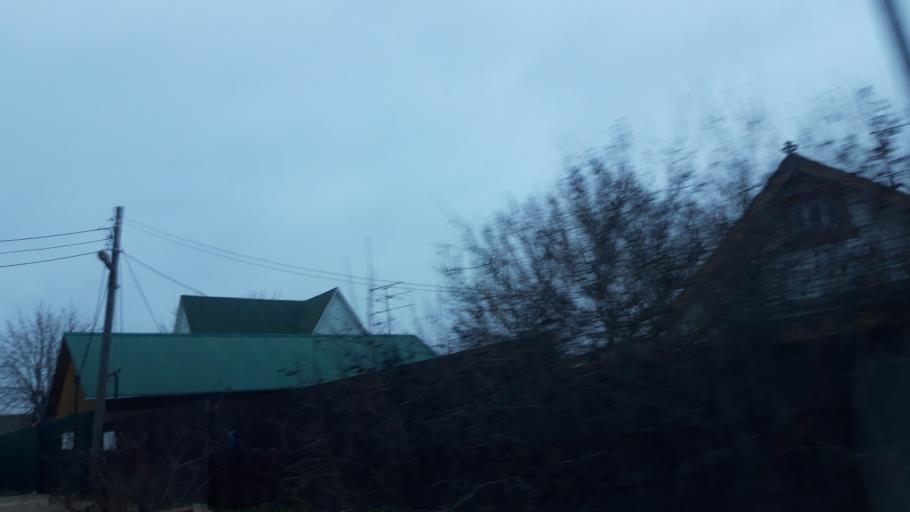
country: RU
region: Moskovskaya
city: Solnechnogorsk
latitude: 56.0798
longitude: 36.9173
